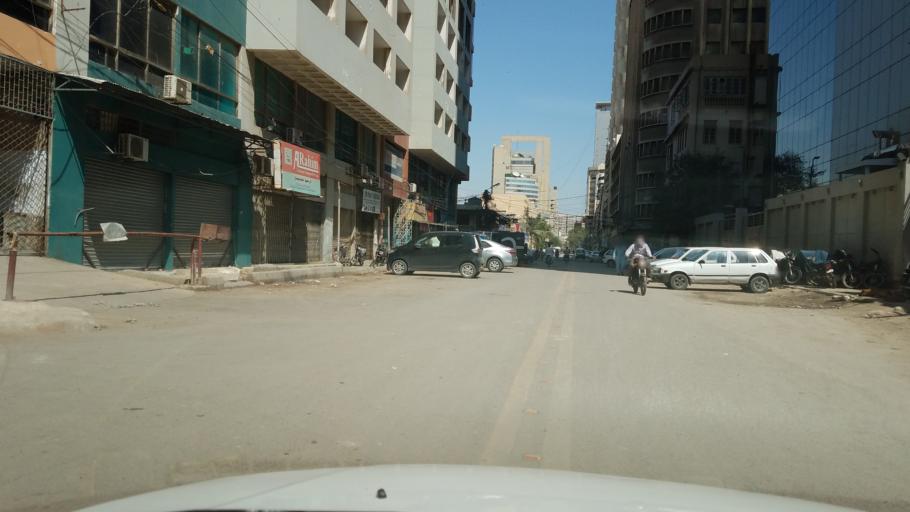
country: PK
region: Sindh
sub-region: Karachi District
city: Karachi
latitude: 24.8500
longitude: 67.0032
